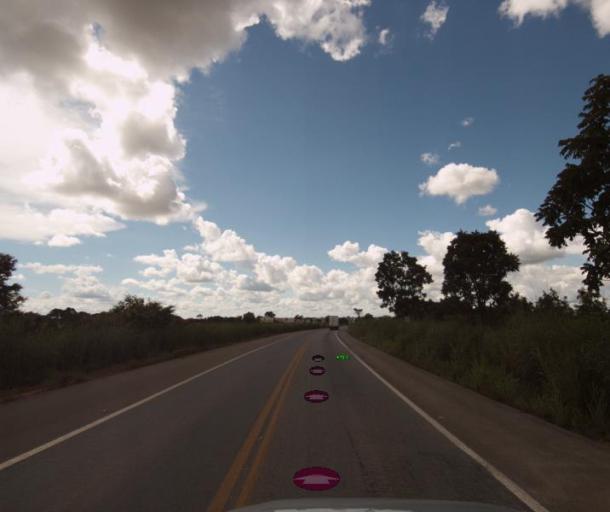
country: BR
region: Goias
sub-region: Porangatu
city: Porangatu
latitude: -13.4873
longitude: -49.1364
